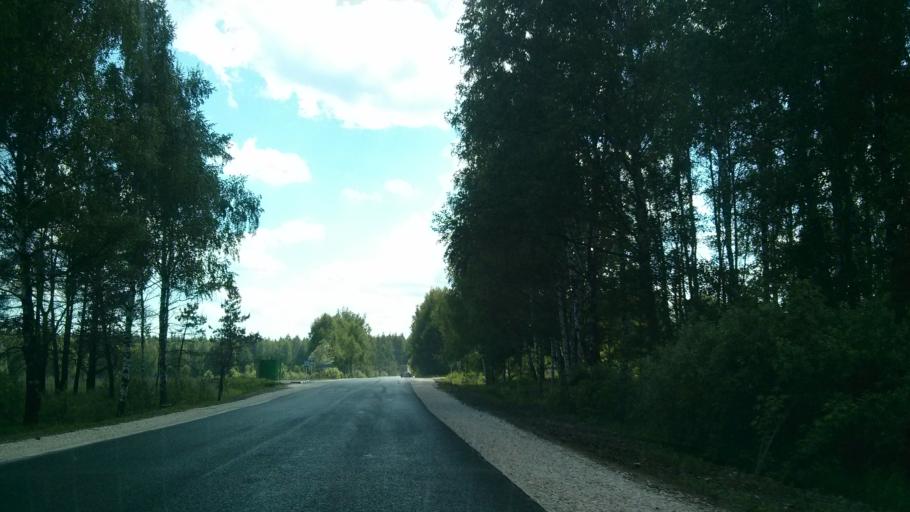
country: RU
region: Vladimir
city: Murom
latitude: 55.5013
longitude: 41.9088
